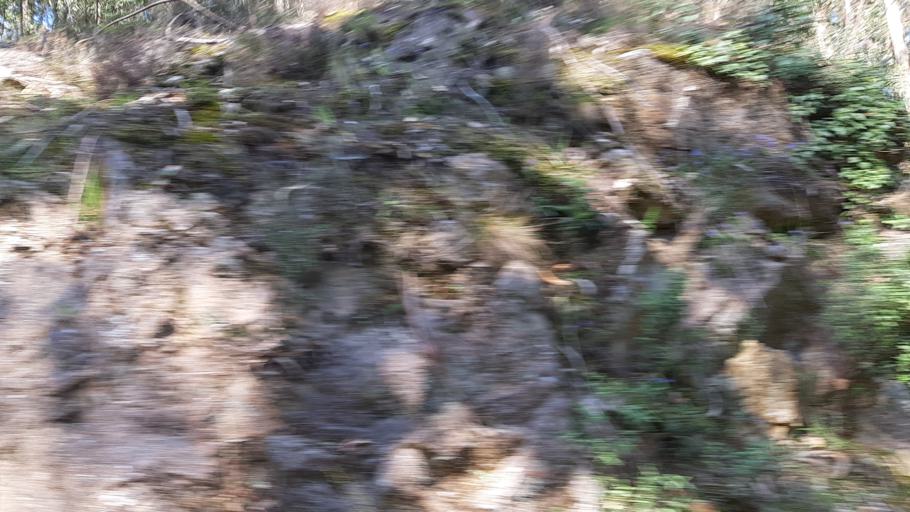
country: ES
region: Galicia
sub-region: Provincia de Pontevedra
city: O Rosal
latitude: 41.9387
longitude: -8.8557
